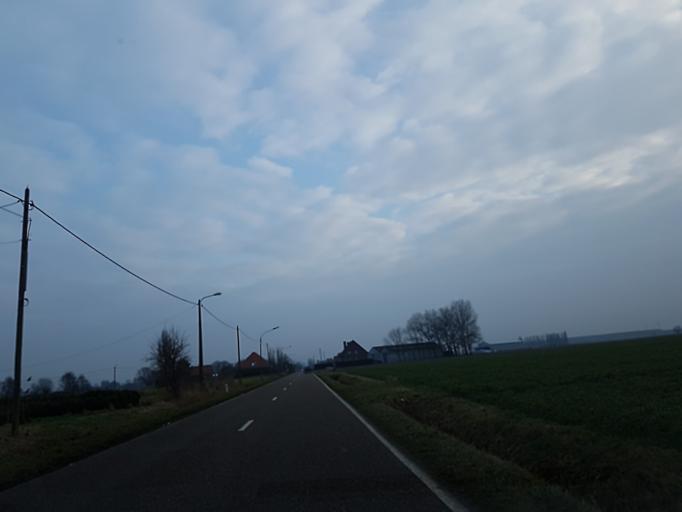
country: BE
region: Flanders
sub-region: Provincie Antwerpen
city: Stabroek
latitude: 51.3185
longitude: 4.3804
